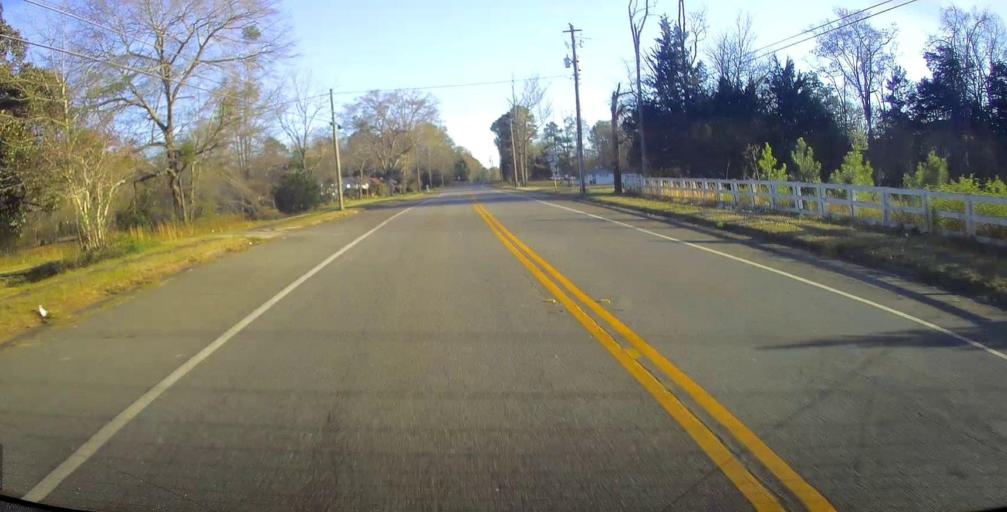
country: US
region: Georgia
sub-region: Talbot County
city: Talbotton
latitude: 32.6674
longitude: -84.5340
